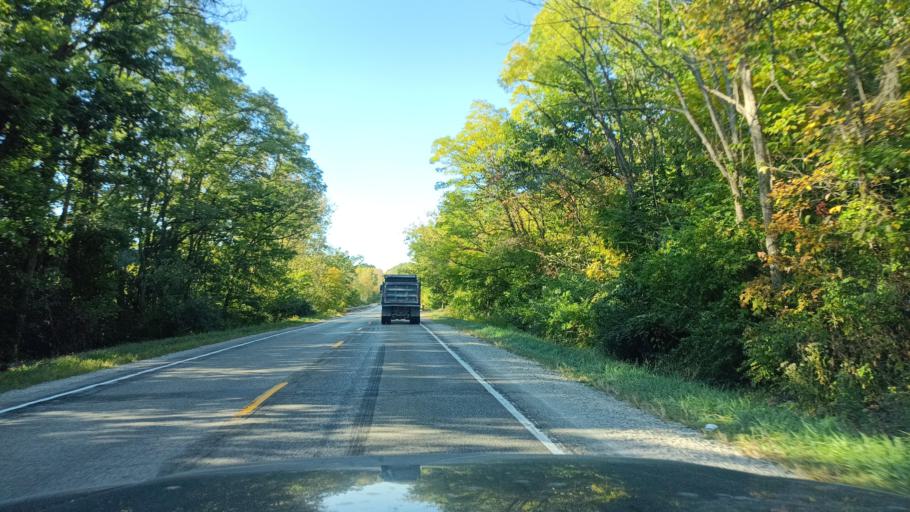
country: US
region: Illinois
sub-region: Clark County
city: Marshall
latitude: 39.4358
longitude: -87.6876
